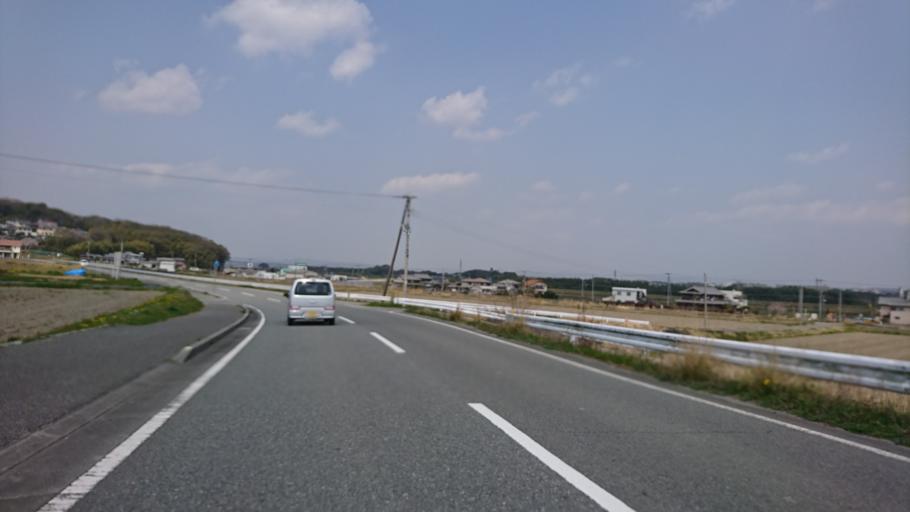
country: JP
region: Hyogo
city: Ono
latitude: 34.8383
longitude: 134.9108
